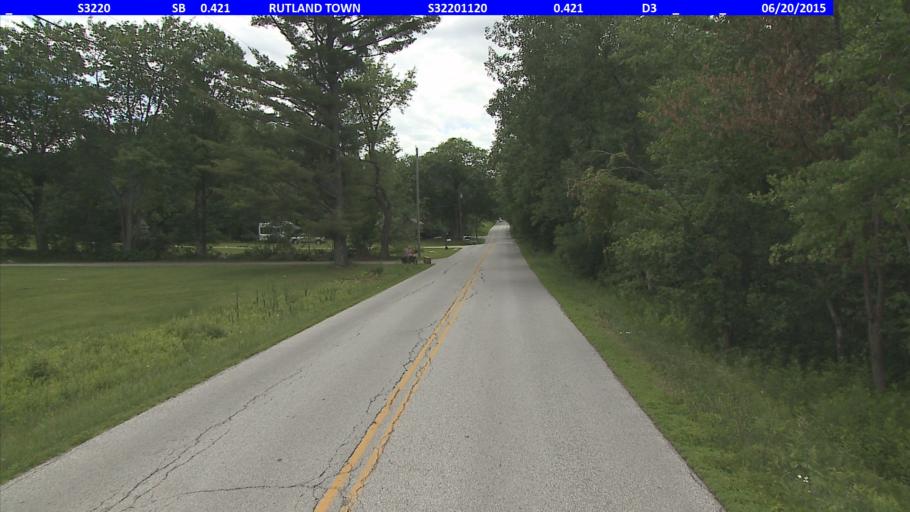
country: US
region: Vermont
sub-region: Rutland County
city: Rutland
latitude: 43.6148
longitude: -72.9364
